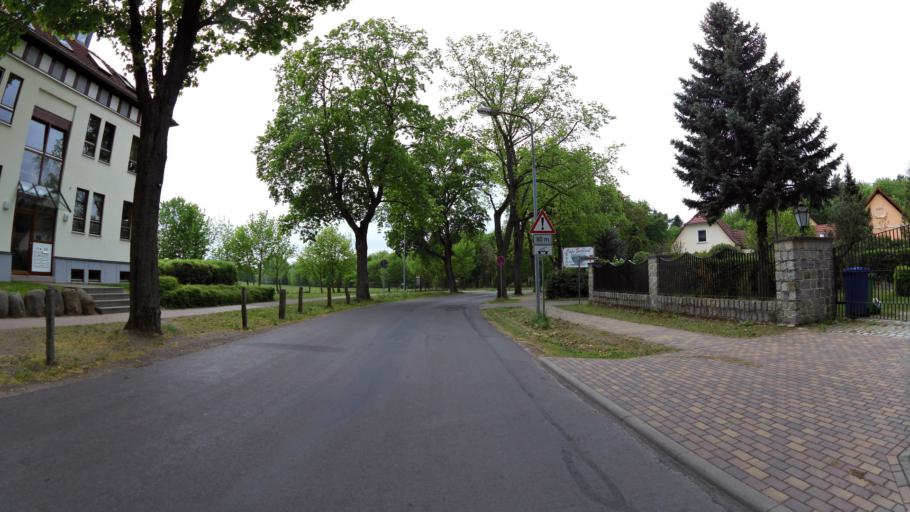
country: DE
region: Brandenburg
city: Schwerin
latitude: 52.2064
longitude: 13.5884
